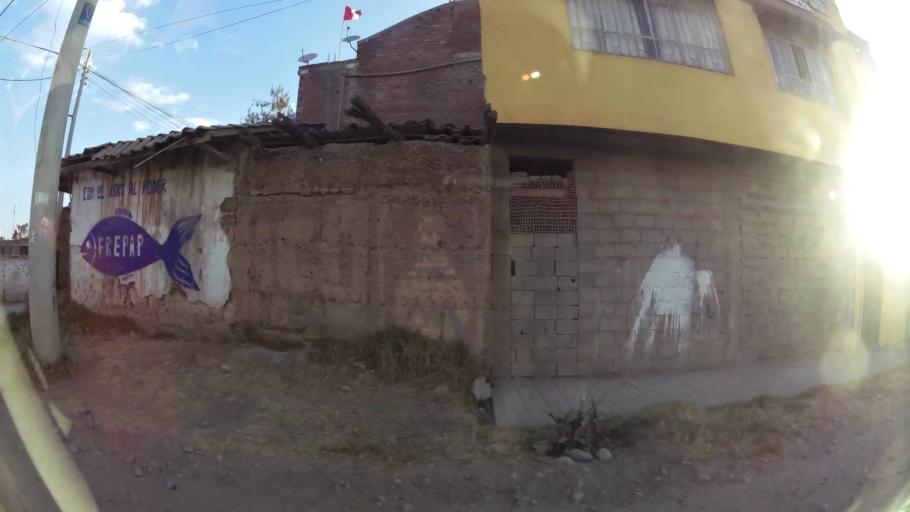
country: PE
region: Junin
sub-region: Provincia de Huancayo
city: Pilcomay
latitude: -12.0382
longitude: -75.2262
